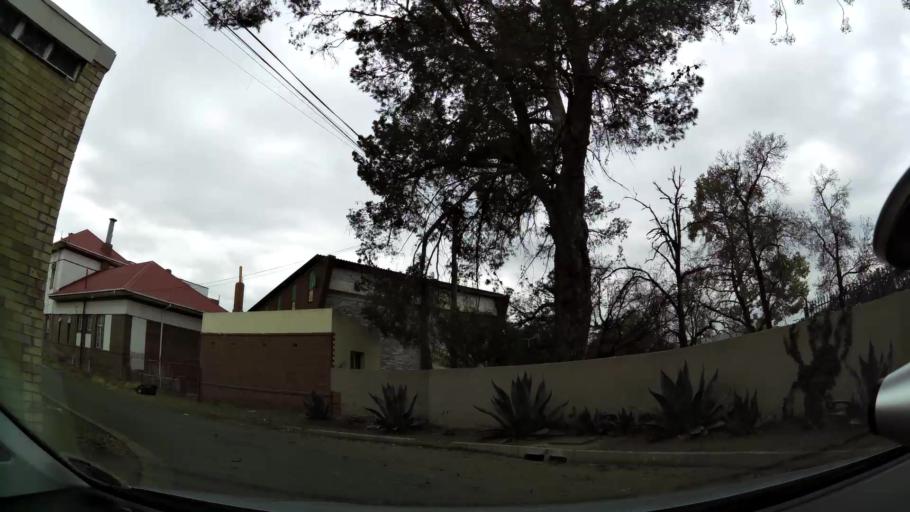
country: ZA
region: Orange Free State
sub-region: Fezile Dabi District Municipality
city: Kroonstad
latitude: -27.6654
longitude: 27.2377
